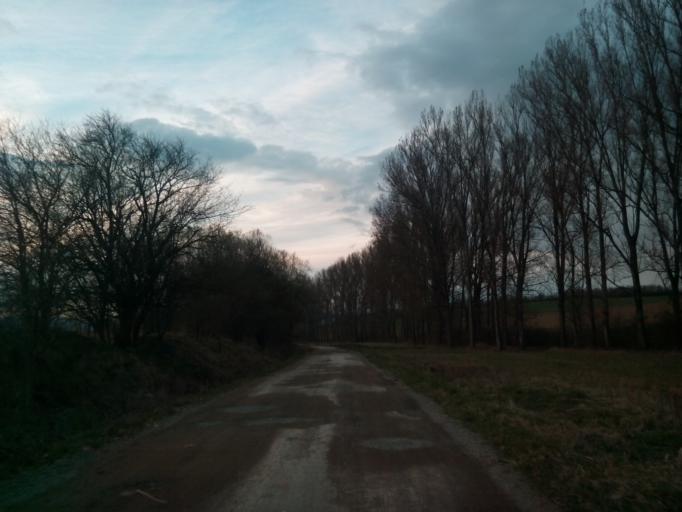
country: SK
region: Kosicky
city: Moldava nad Bodvou
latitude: 48.5463
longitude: 20.9832
